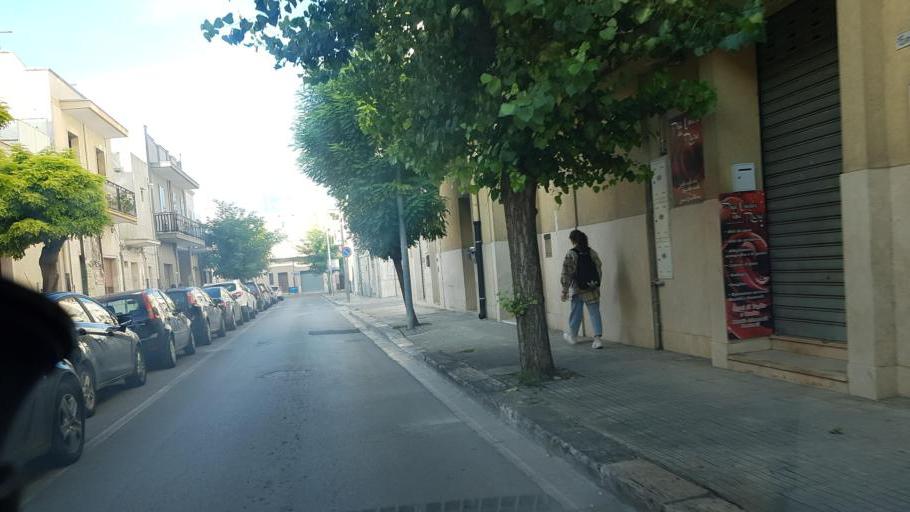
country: IT
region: Apulia
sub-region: Provincia di Brindisi
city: Francavilla Fontana
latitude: 40.5315
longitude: 17.5866
